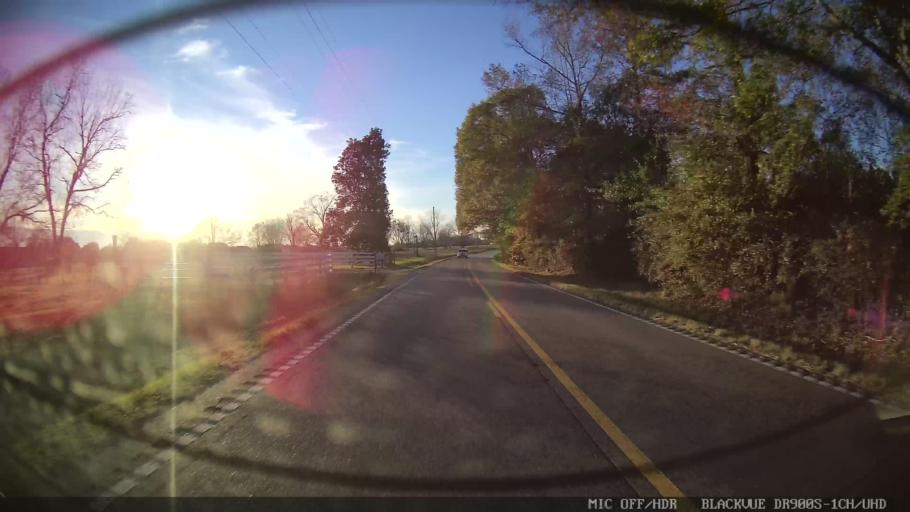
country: US
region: Mississippi
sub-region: Lamar County
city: Lumberton
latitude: 30.9960
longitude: -89.3900
